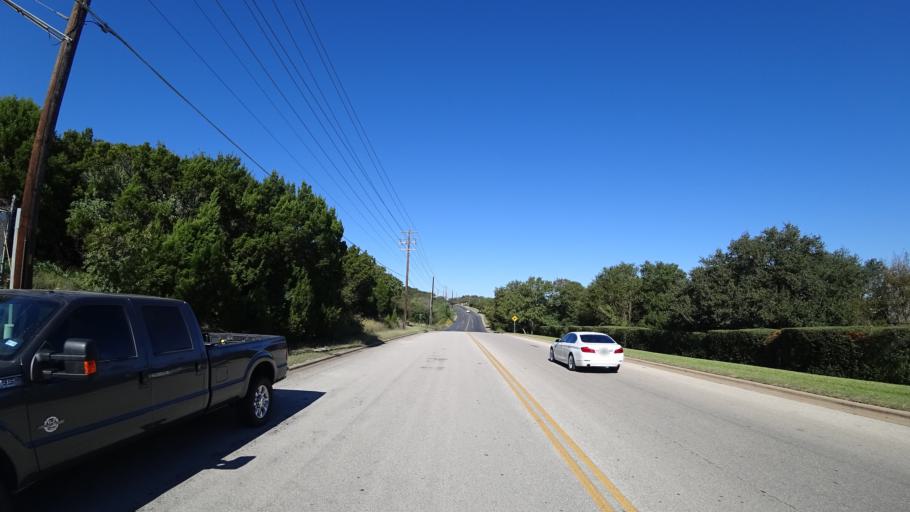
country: US
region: Texas
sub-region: Travis County
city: West Lake Hills
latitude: 30.3326
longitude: -97.7914
